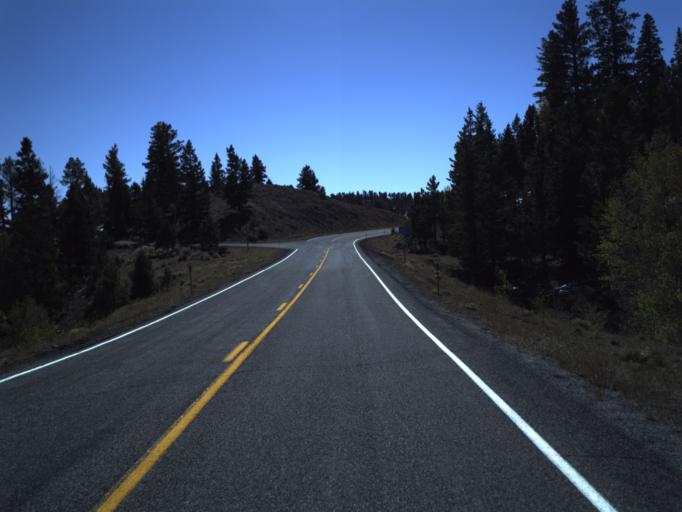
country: US
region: Utah
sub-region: Wayne County
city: Loa
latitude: 38.1339
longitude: -111.3276
